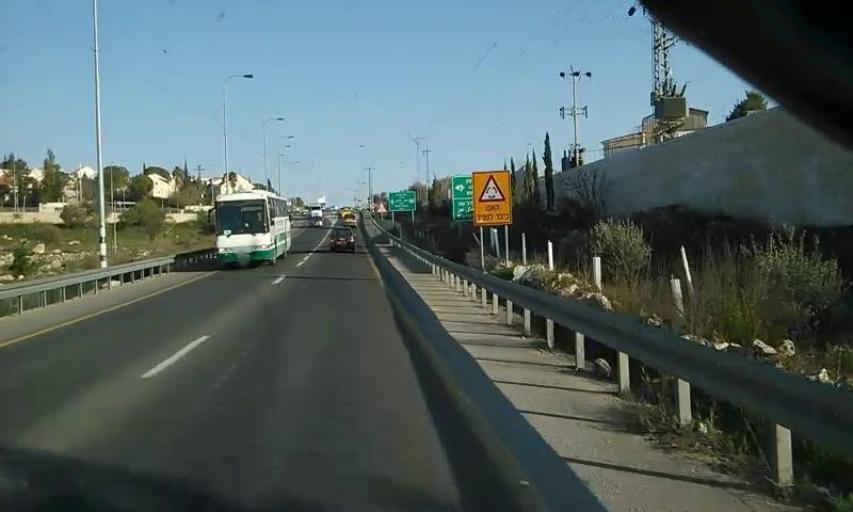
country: PS
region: West Bank
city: Jurat ash Sham`ah
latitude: 31.6489
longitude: 35.1460
